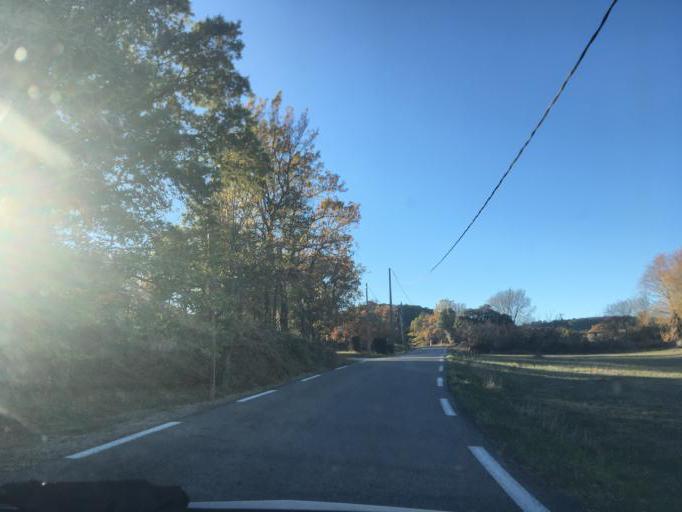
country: FR
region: Provence-Alpes-Cote d'Azur
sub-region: Departement du Var
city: Flayosc
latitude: 43.6032
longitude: 6.3550
